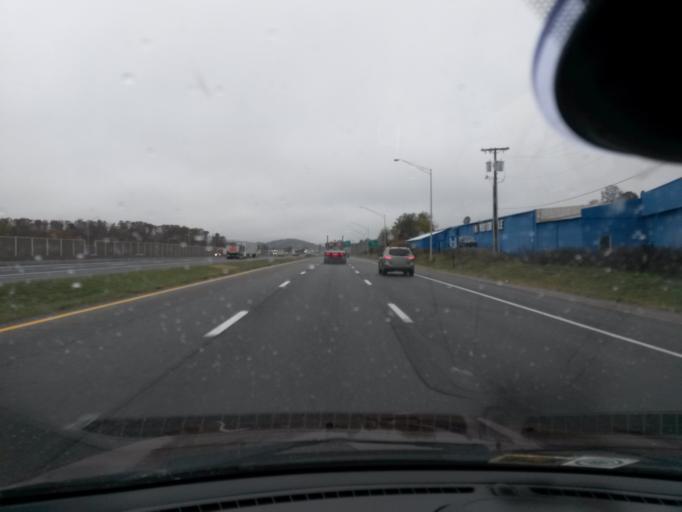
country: US
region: Virginia
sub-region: Montgomery County
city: Christiansburg
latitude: 37.1335
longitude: -80.3616
